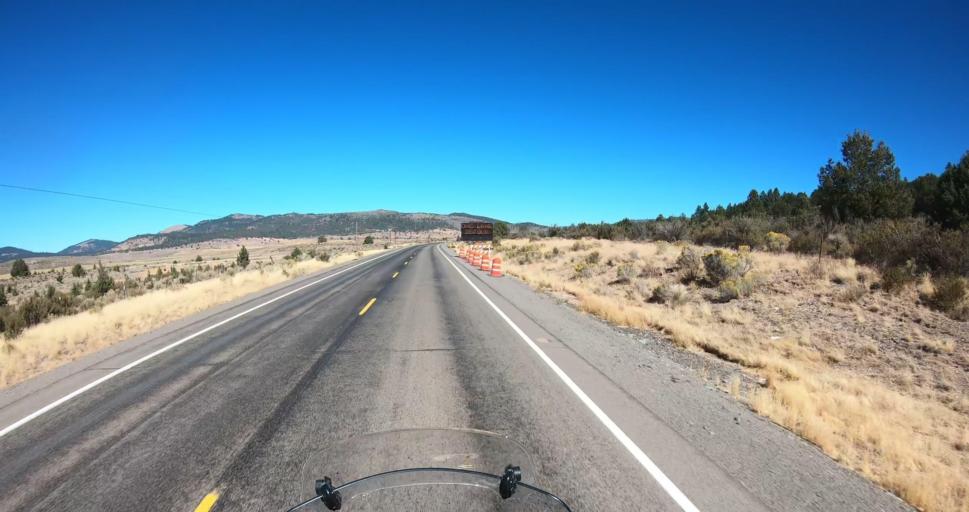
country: US
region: Oregon
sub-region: Lake County
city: Lakeview
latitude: 42.3075
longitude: -120.3416
